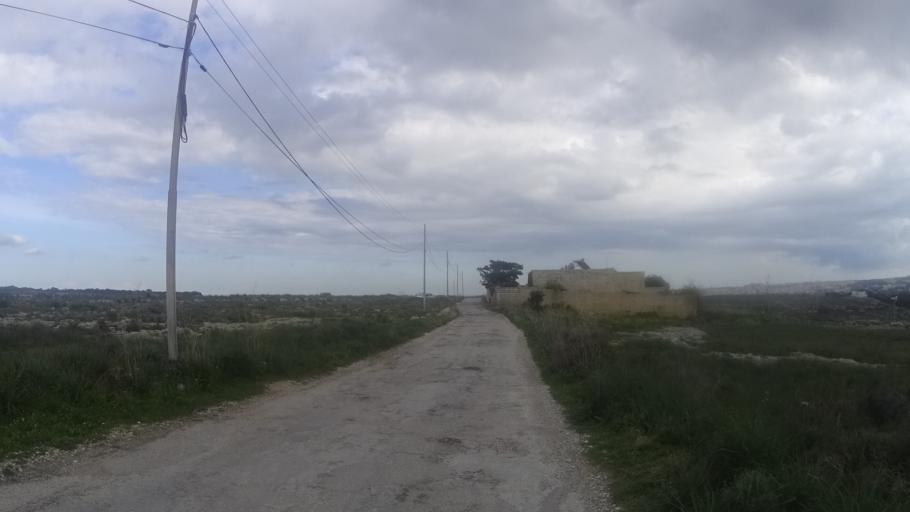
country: MT
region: L-Imgarr
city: Imgarr
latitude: 35.9008
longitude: 14.3744
